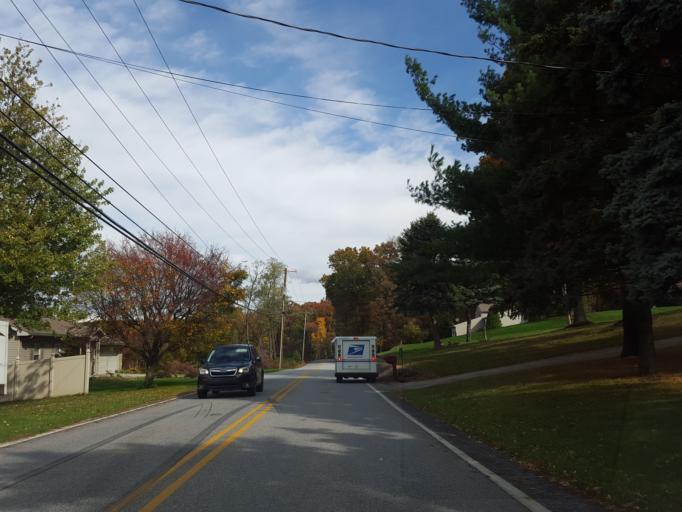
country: US
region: Pennsylvania
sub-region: York County
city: Windsor
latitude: 39.9427
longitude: -76.6022
